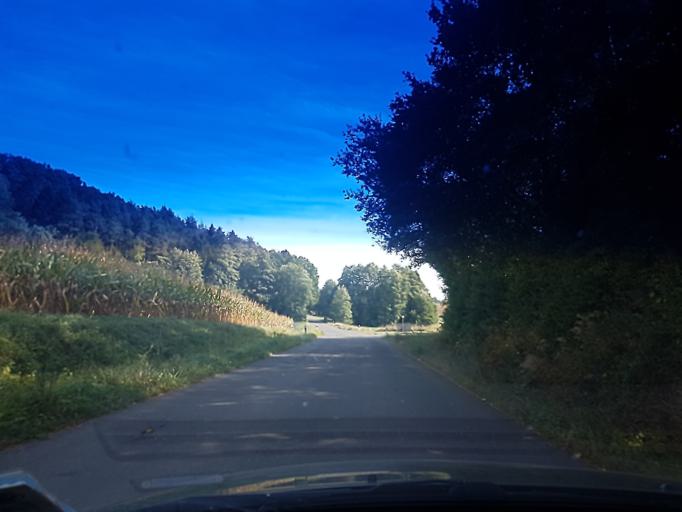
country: DE
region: Bavaria
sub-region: Upper Franconia
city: Schlusselfeld
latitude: 49.7739
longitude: 10.6037
